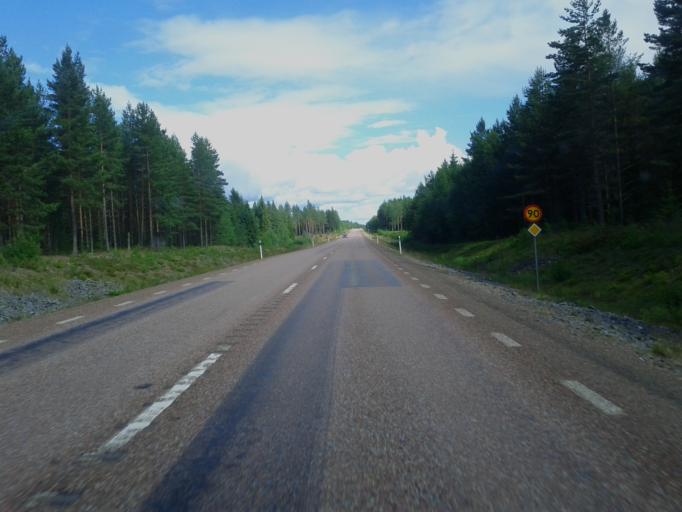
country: SE
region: Dalarna
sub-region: Rattviks Kommun
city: Raettvik
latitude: 60.8457
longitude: 15.1596
